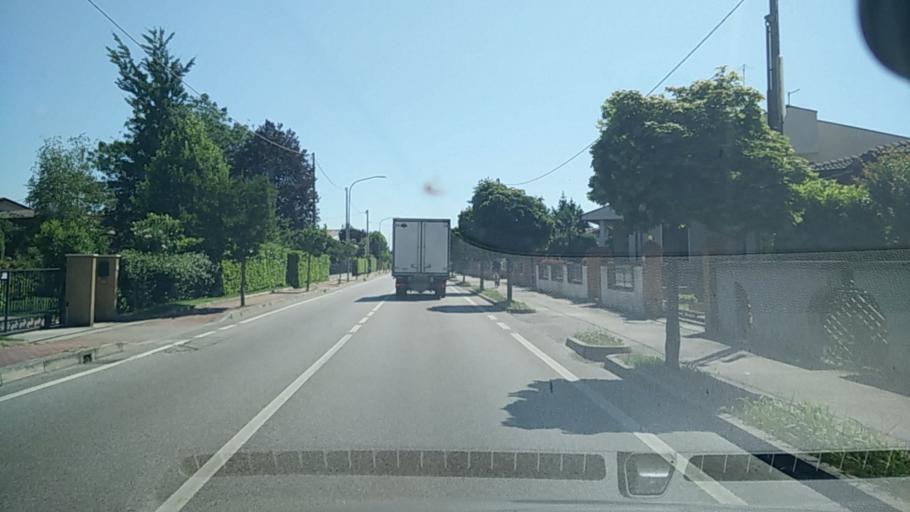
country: IT
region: Veneto
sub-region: Provincia di Venezia
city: Camponogara
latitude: 45.3834
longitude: 12.0847
